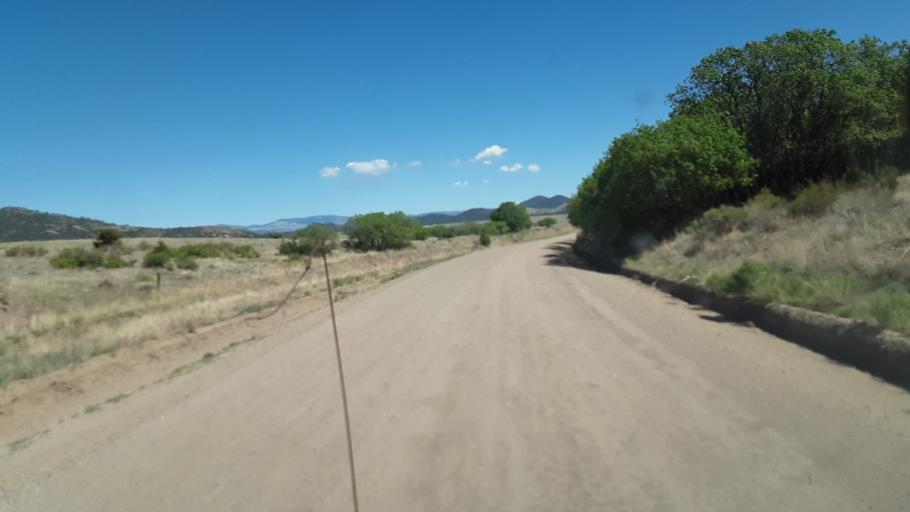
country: US
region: Colorado
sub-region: Custer County
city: Westcliffe
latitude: 38.2439
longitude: -105.5011
